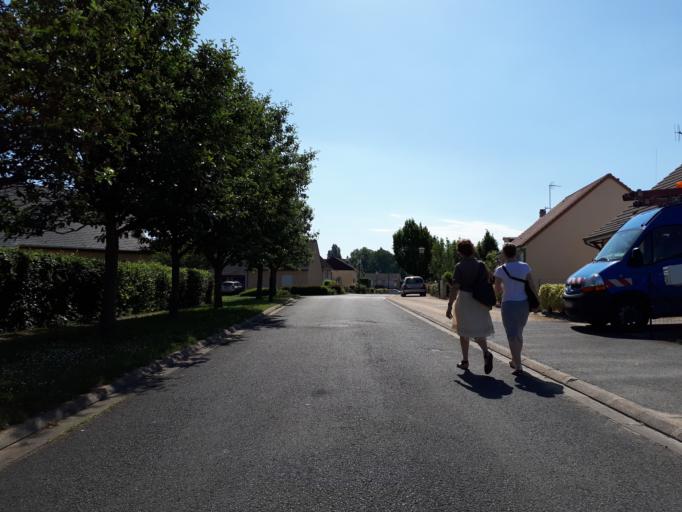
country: FR
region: Pays de la Loire
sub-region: Departement de la Sarthe
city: Champagne
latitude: 48.0766
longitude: 0.2921
